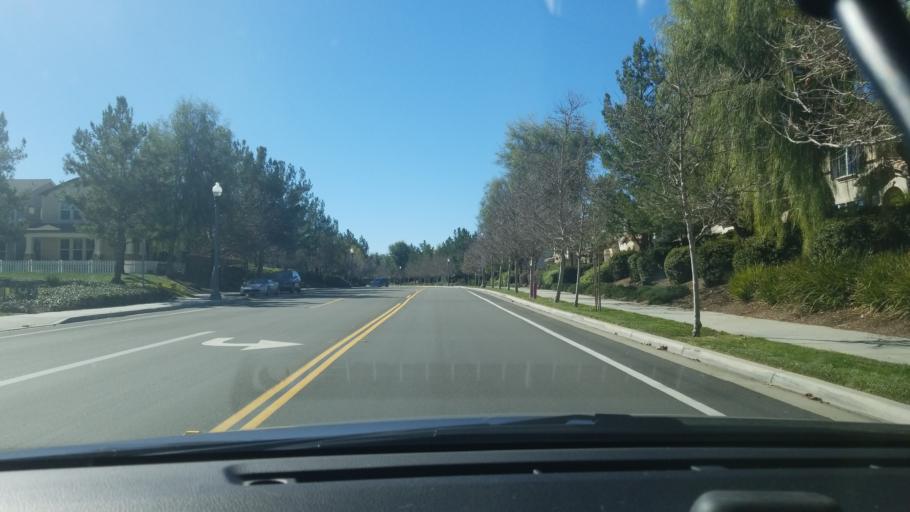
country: US
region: California
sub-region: Riverside County
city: Murrieta Hot Springs
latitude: 33.5396
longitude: -117.1590
